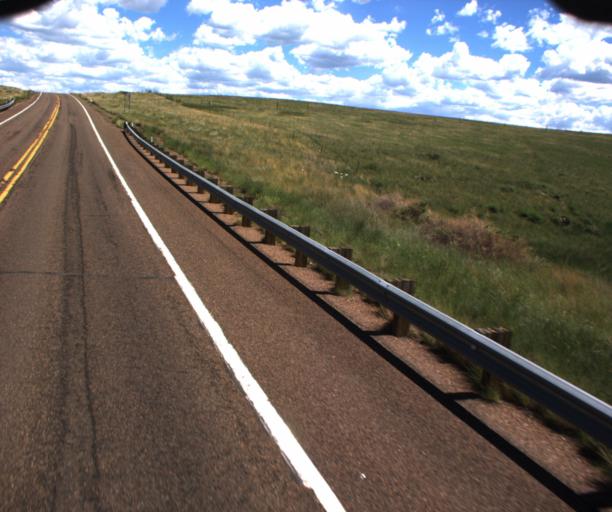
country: US
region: Arizona
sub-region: Apache County
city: Springerville
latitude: 34.1993
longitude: -109.3946
